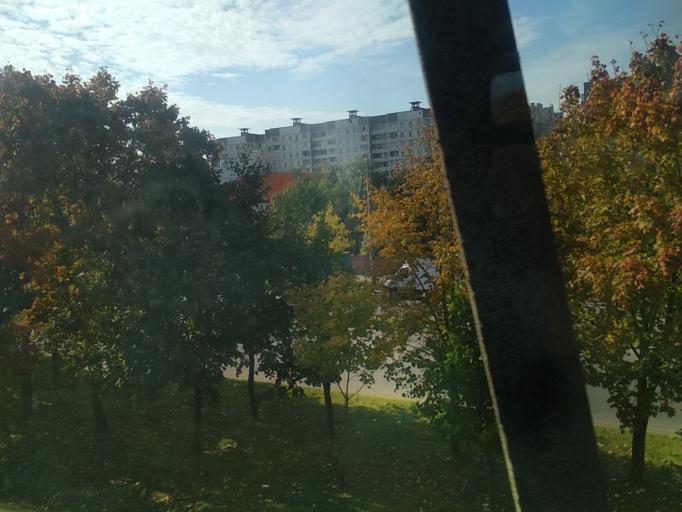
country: BY
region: Minsk
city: Minsk
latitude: 53.8793
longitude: 27.5629
